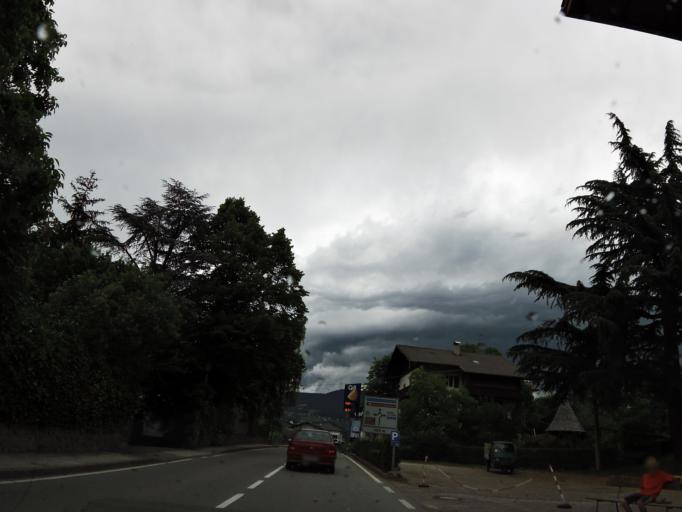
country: IT
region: Trentino-Alto Adige
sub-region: Bolzano
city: Fie Allo Sciliar
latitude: 46.5171
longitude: 11.5049
